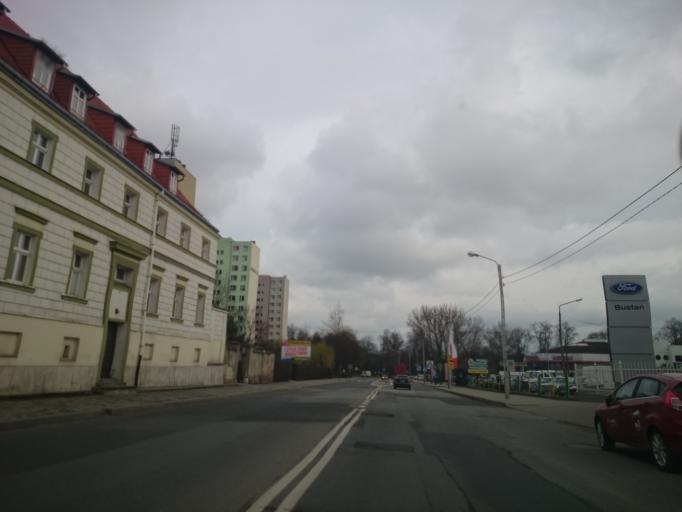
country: PL
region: Opole Voivodeship
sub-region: Powiat nyski
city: Nysa
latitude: 50.4785
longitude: 17.3206
